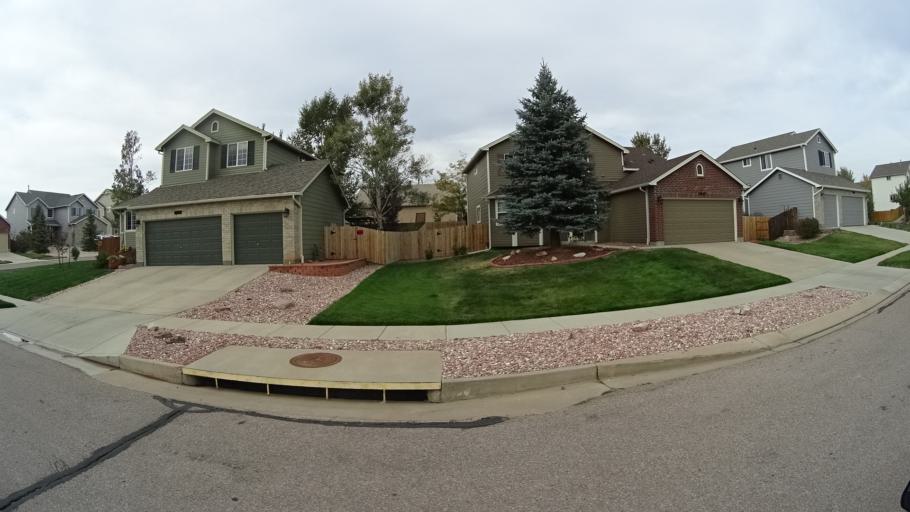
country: US
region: Colorado
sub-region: El Paso County
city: Cimarron Hills
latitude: 38.9213
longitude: -104.7041
